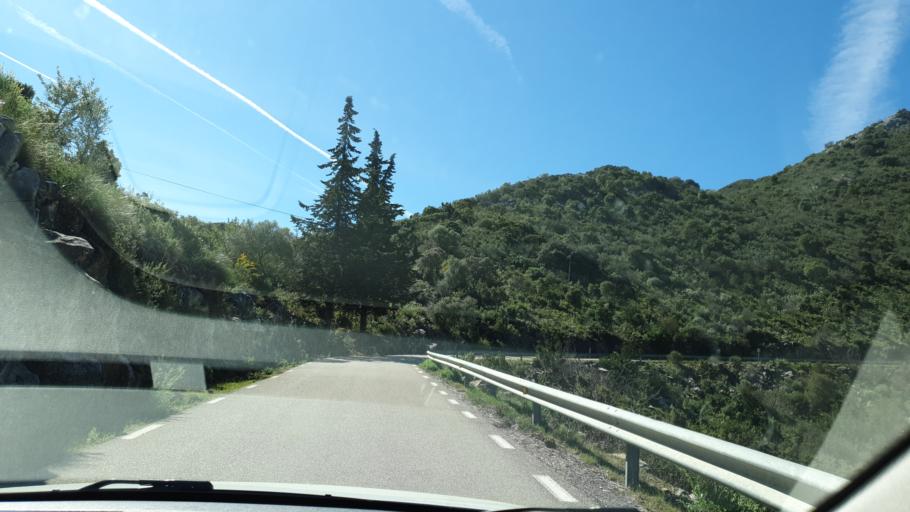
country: ES
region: Andalusia
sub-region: Provincia de Malaga
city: Ojen
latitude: 36.5912
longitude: -4.8727
